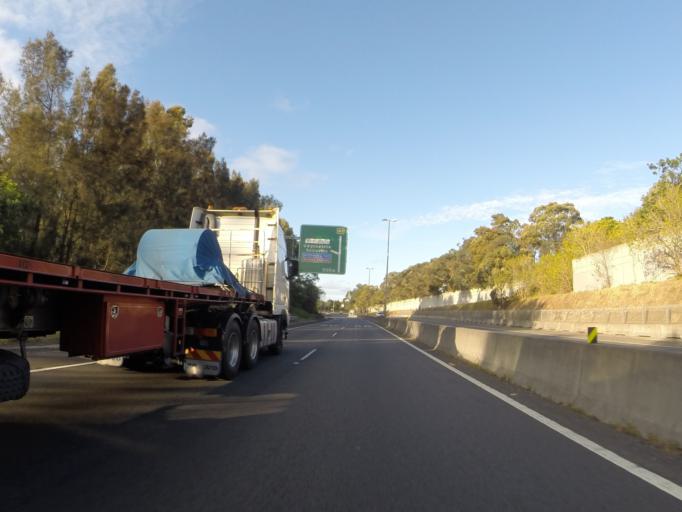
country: AU
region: New South Wales
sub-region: Wollongong
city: Gwynneville
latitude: -34.4151
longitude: 150.8809
